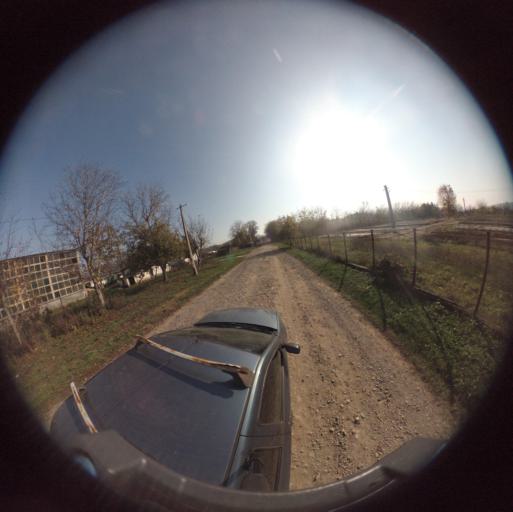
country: RO
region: Vaslui
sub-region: Comuna Dumesti
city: Dumesti
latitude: 46.8290
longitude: 27.2645
